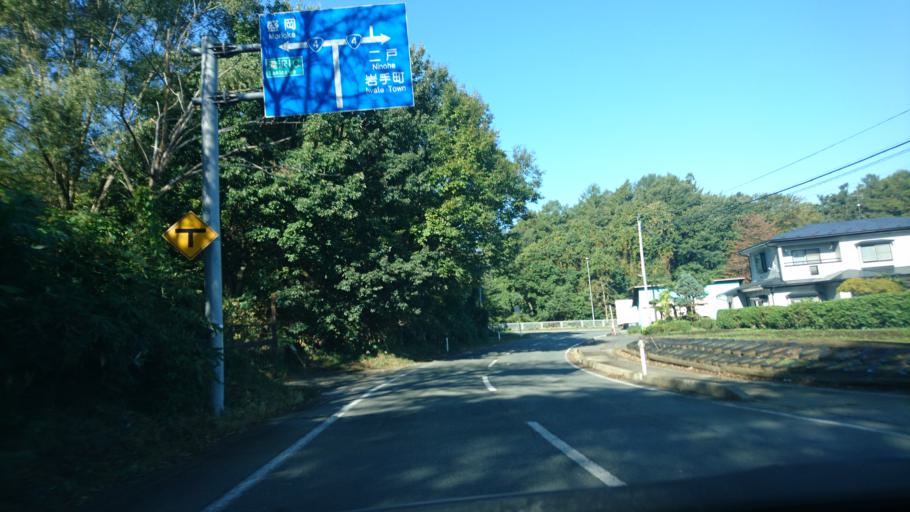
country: JP
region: Iwate
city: Morioka-shi
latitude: 39.8116
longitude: 141.1312
